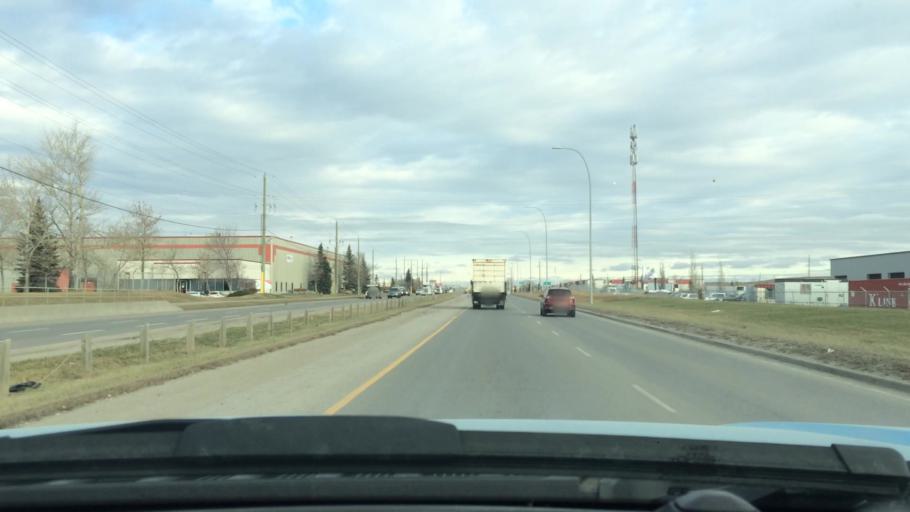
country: CA
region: Alberta
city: Calgary
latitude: 51.0043
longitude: -113.9584
